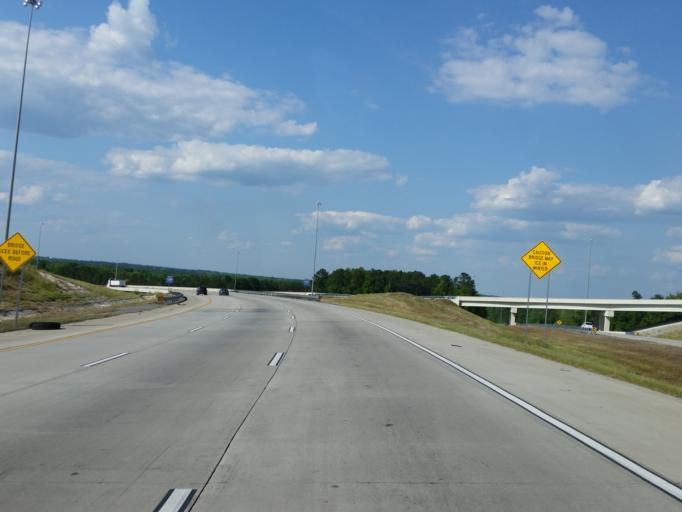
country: US
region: Georgia
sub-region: Bibb County
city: West Point
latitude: 32.7553
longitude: -83.7098
